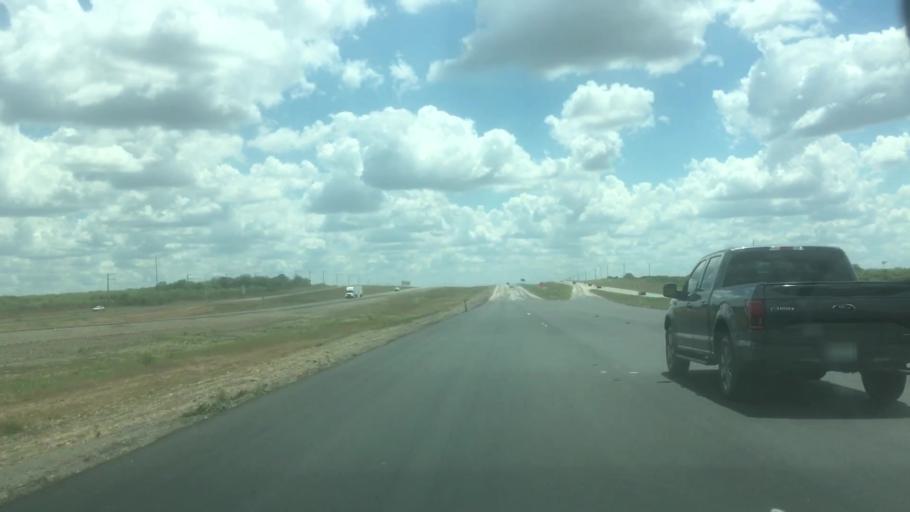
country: US
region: Texas
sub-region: Caldwell County
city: Lockhart
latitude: 29.9872
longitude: -97.6832
